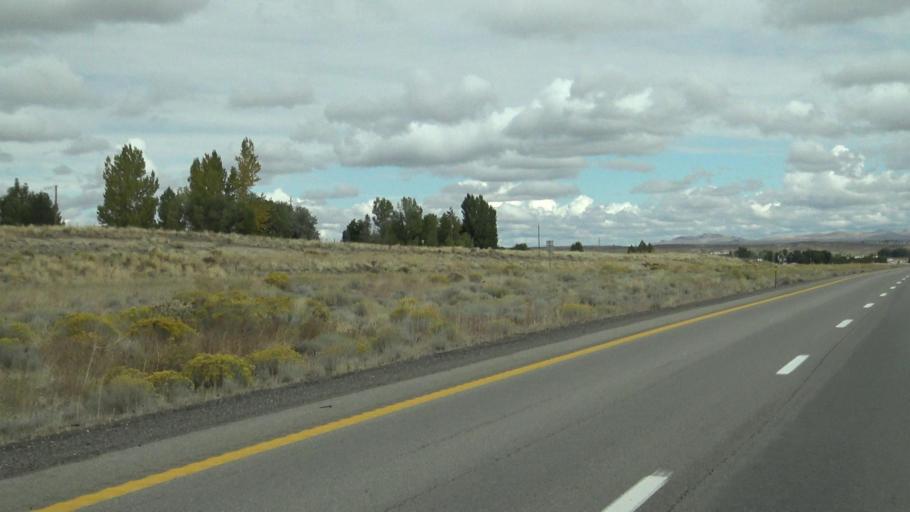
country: US
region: Nevada
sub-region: Elko County
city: Elko
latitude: 40.9293
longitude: -115.6723
